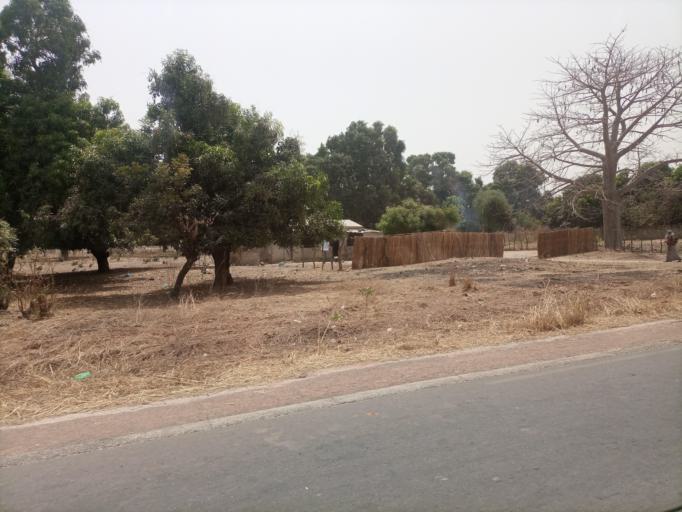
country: SN
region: Fatick
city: Sokone
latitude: 13.7279
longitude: -16.4227
